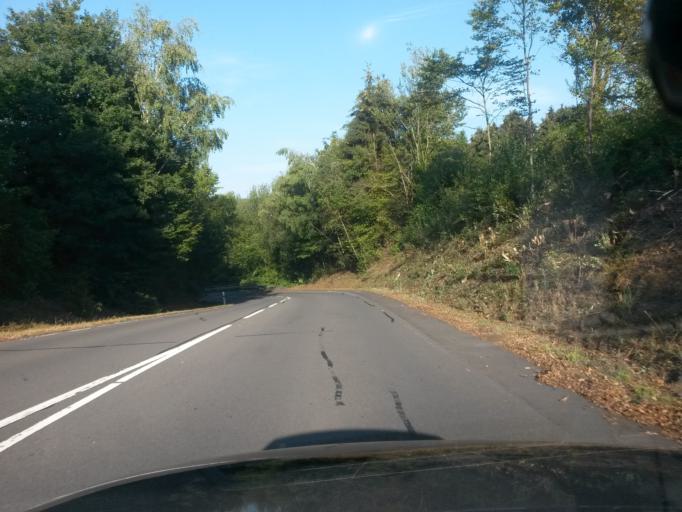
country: DE
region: North Rhine-Westphalia
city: Wiehl
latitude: 50.9587
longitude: 7.5506
